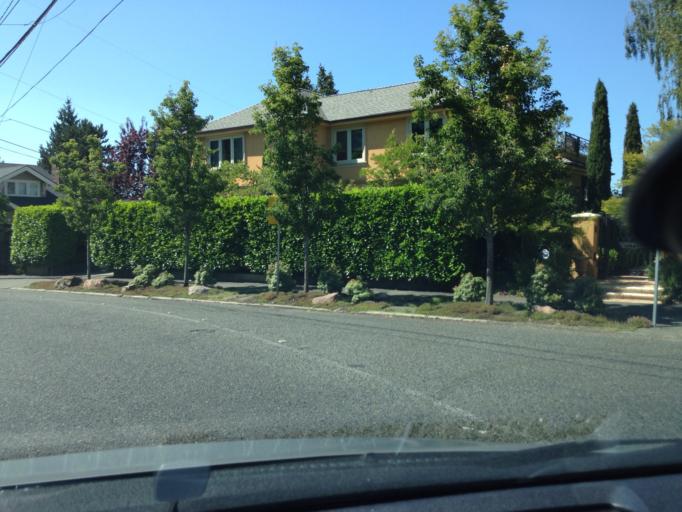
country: US
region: Washington
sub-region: King County
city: Seattle
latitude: 47.6382
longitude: -122.3147
